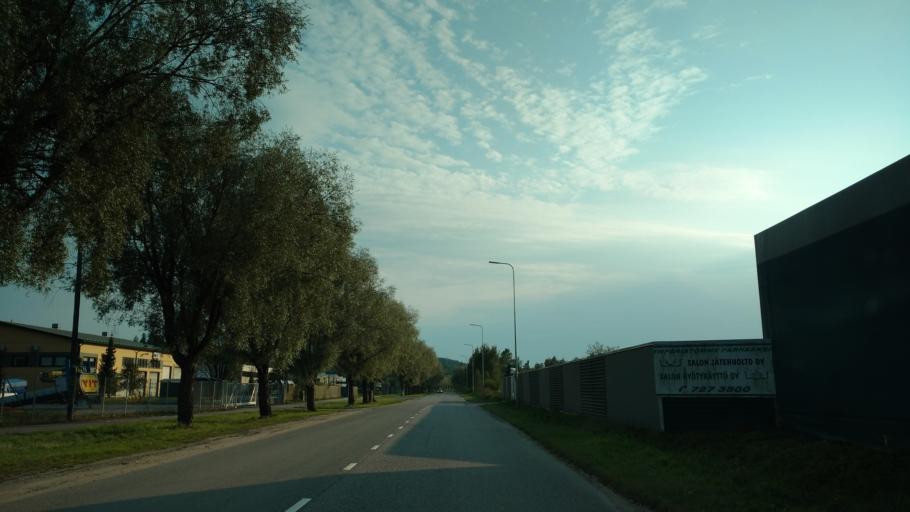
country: FI
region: Varsinais-Suomi
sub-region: Salo
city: Salo
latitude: 60.3733
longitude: 23.1054
